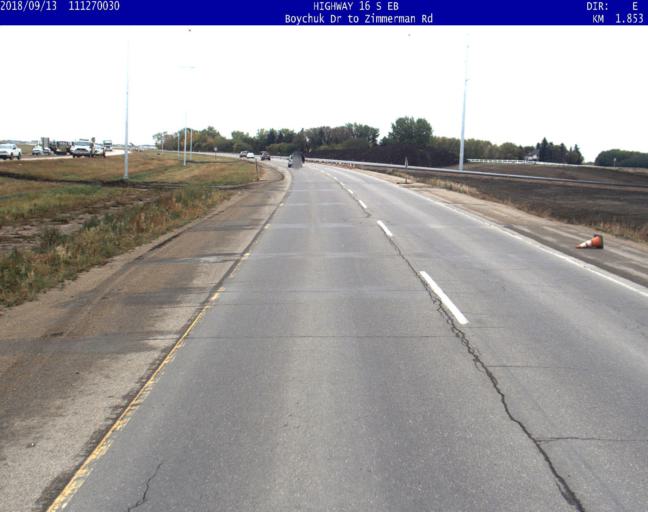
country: CA
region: Saskatchewan
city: Saskatoon
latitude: 52.0866
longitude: -106.5714
